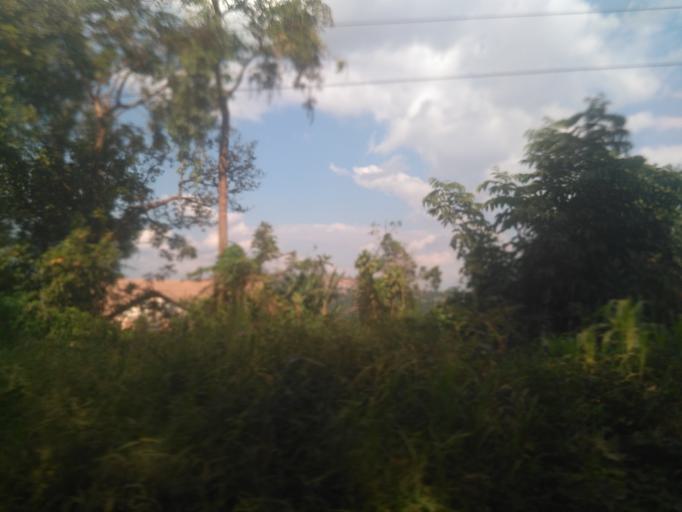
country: UG
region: Central Region
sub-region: Wakiso District
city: Kajansi
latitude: 0.2654
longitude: 32.4375
